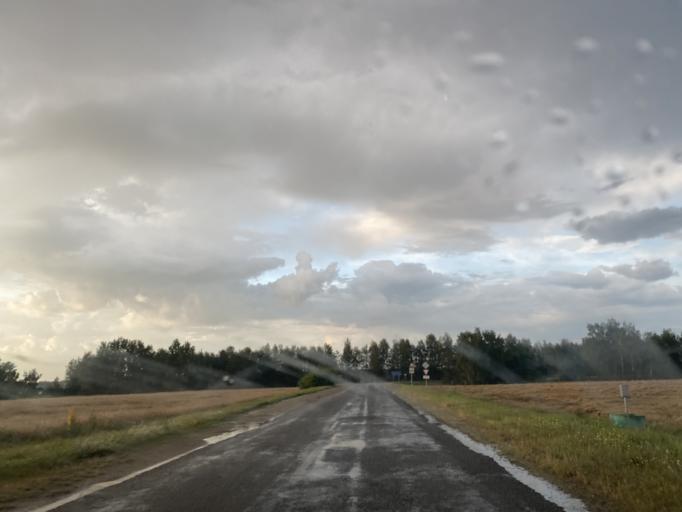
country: BY
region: Brest
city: Tsyelyakhany
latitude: 52.5572
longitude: 25.6387
